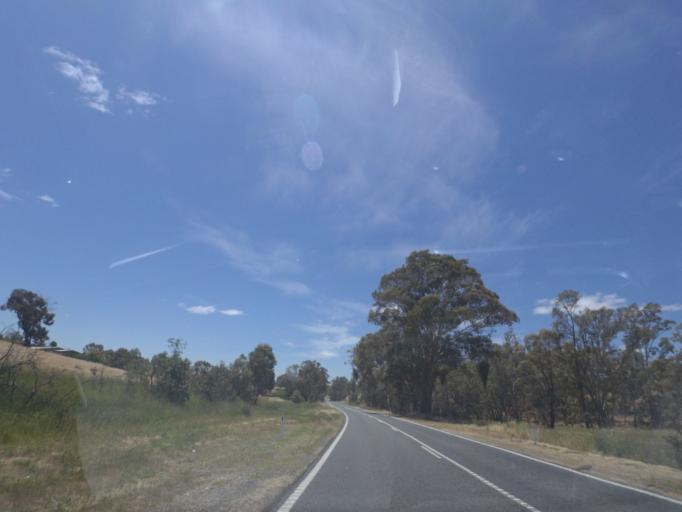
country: AU
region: Victoria
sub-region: Mount Alexander
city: Castlemaine
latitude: -37.1995
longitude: 144.1459
